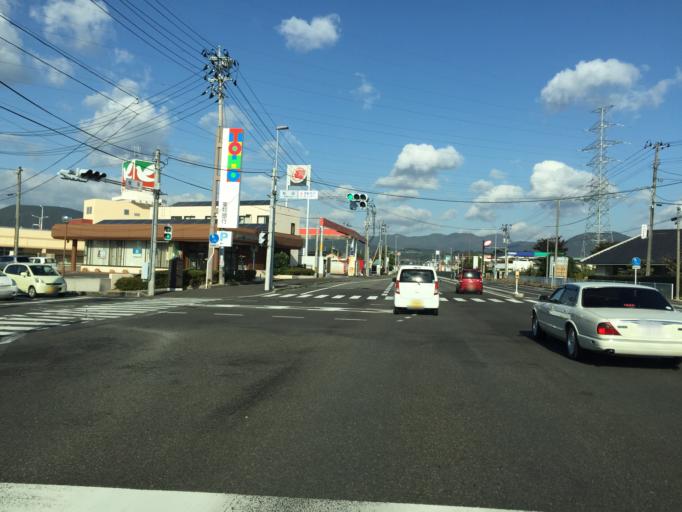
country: JP
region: Fukushima
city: Fukushima-shi
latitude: 37.8060
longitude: 140.4503
